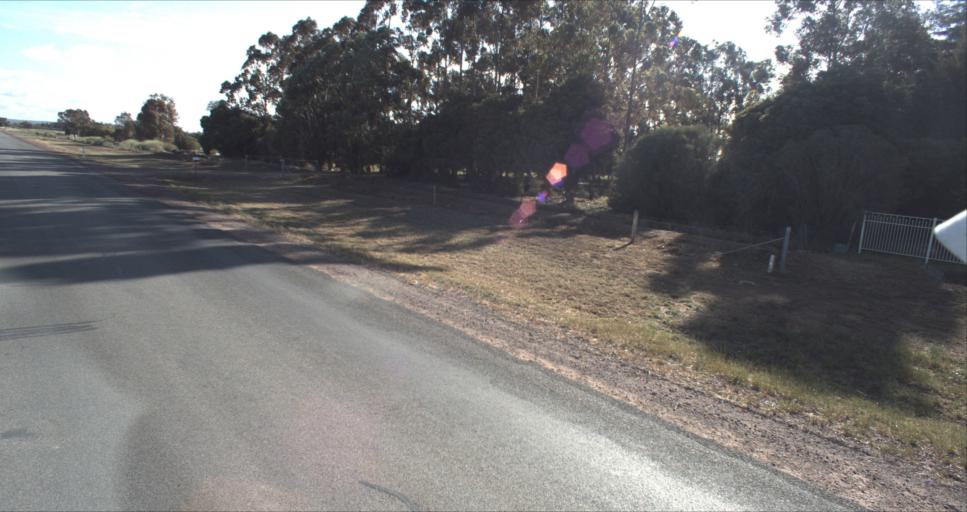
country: AU
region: New South Wales
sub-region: Leeton
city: Leeton
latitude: -34.5293
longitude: 146.3890
